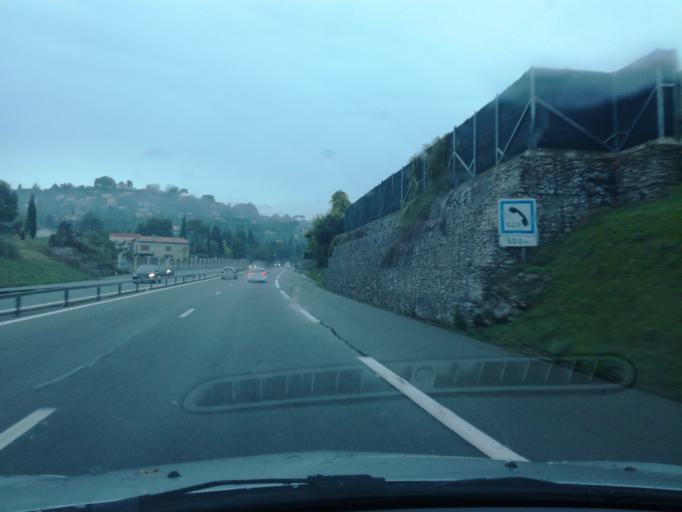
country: FR
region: Provence-Alpes-Cote d'Azur
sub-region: Departement des Alpes-Maritimes
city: Mougins
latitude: 43.5914
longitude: 7.0006
